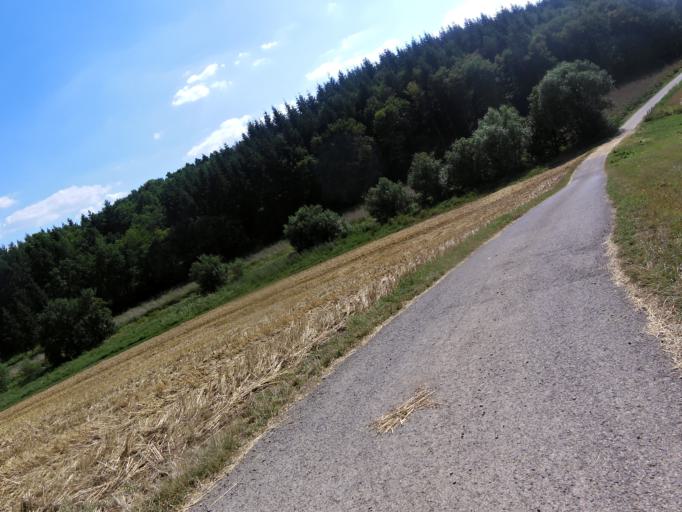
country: DE
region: Bavaria
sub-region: Regierungsbezirk Unterfranken
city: Gadheim
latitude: 49.8458
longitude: 9.9156
